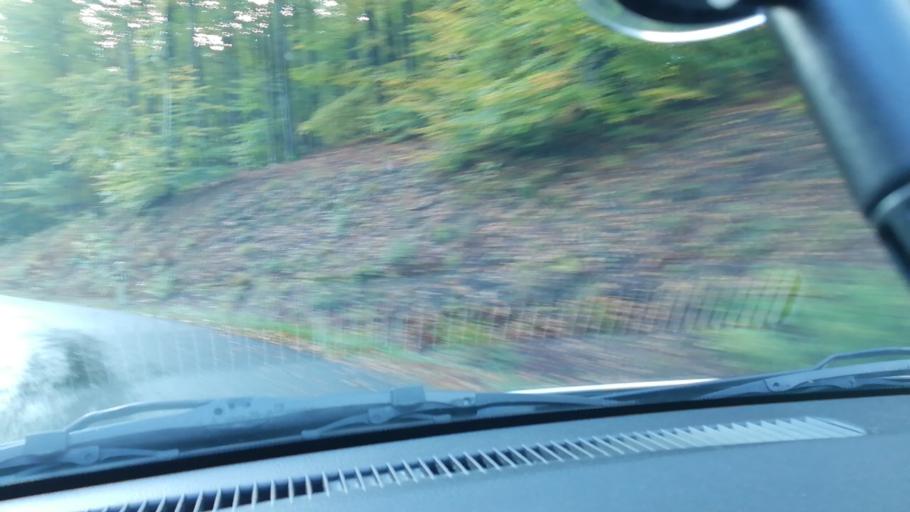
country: DE
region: Bavaria
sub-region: Regierungsbezirk Unterfranken
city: Neuhutten
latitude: 49.9698
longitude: 9.4495
